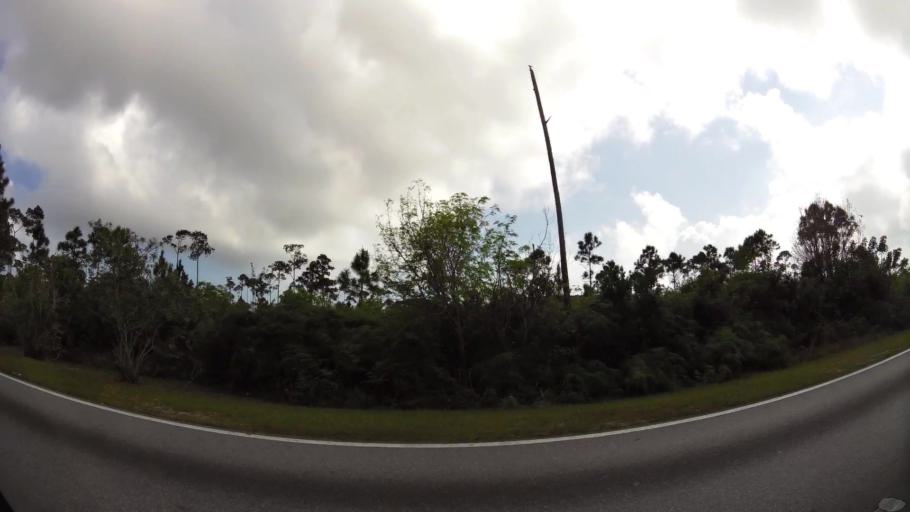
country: BS
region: Freeport
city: Freeport
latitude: 26.5171
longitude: -78.7033
